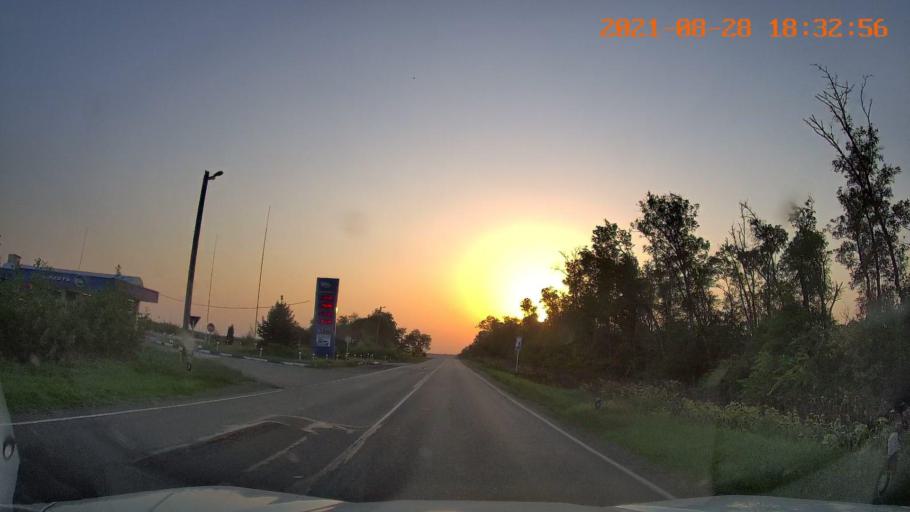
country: RU
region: Adygeya
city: Giaginskaya
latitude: 44.8773
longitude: 40.1866
